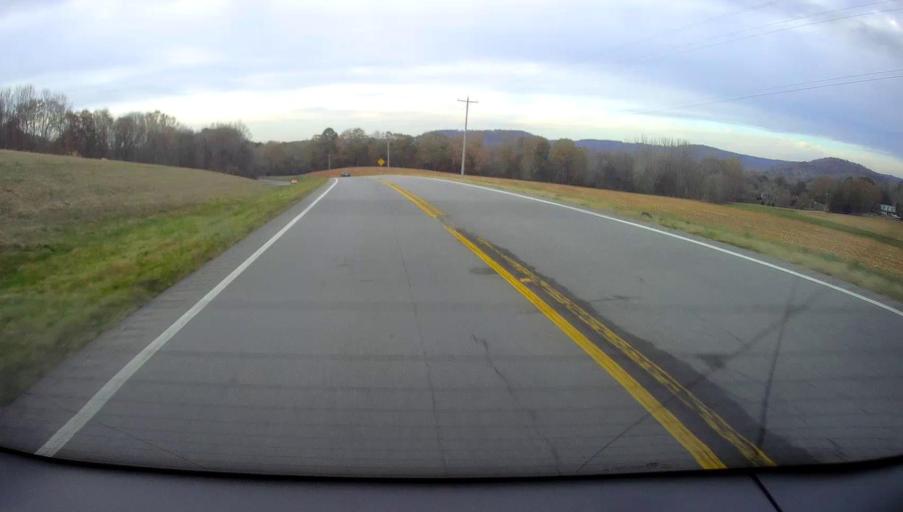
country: US
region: Alabama
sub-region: Marshall County
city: Arab
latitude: 34.3817
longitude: -86.6574
